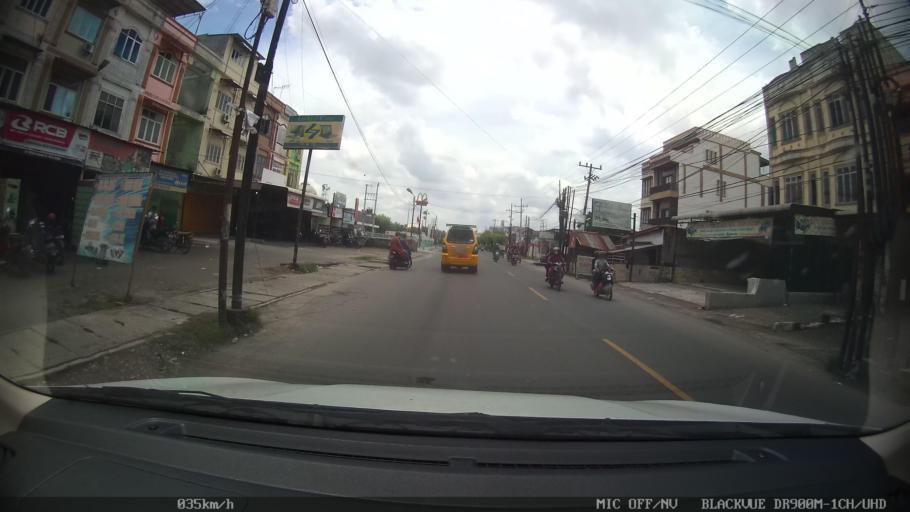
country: ID
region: North Sumatra
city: Medan
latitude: 3.6189
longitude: 98.7074
